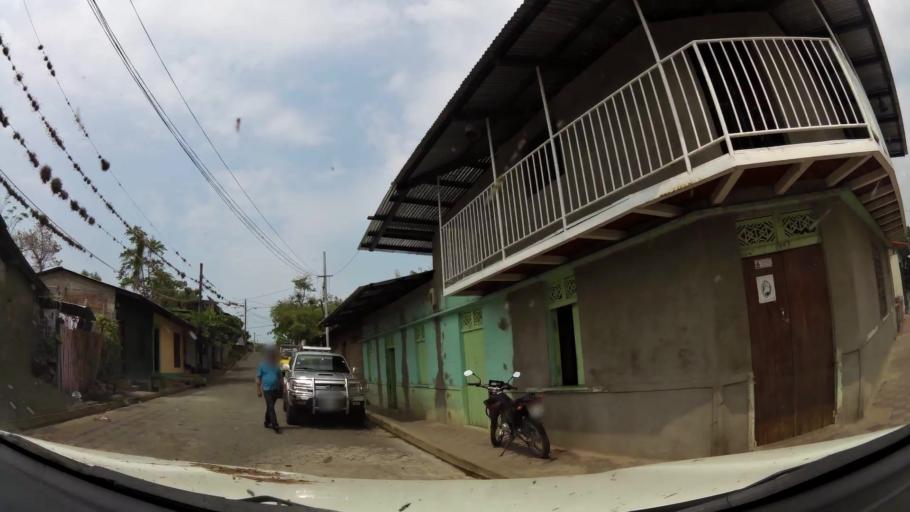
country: NI
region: Granada
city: Diria
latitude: 11.8848
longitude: -86.0542
